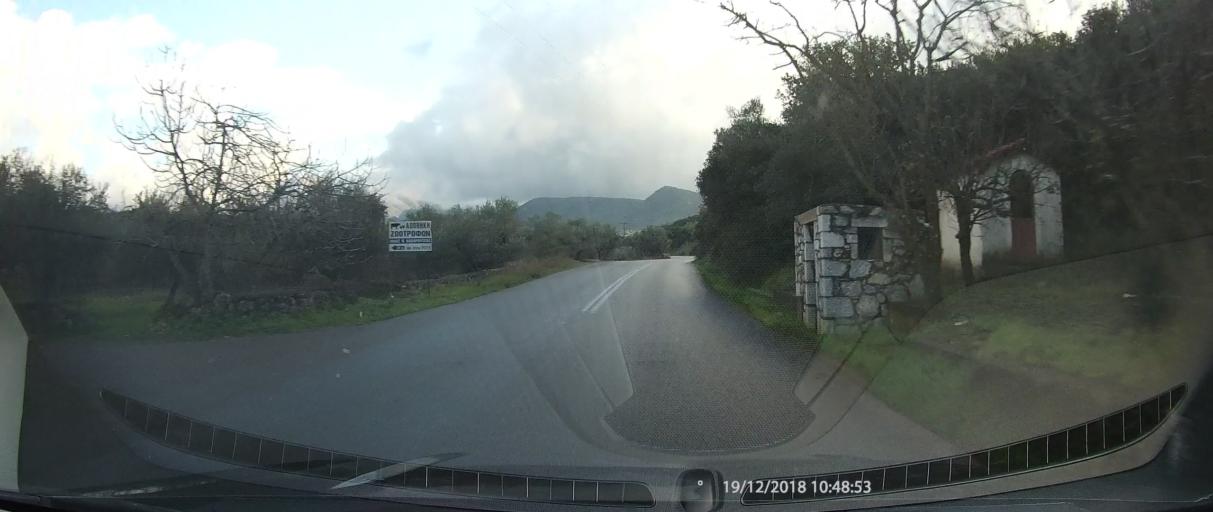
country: GR
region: Peloponnese
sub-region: Nomos Messinias
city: Kardamyli
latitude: 36.9282
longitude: 22.1924
